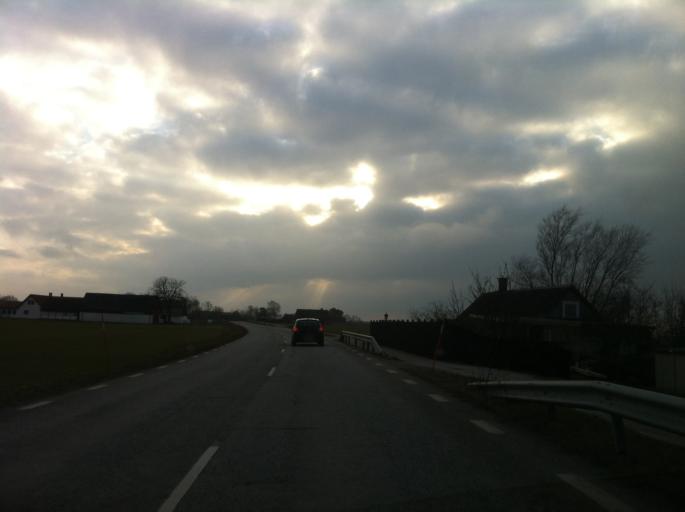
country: SE
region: Skane
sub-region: Kavlinge Kommun
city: Kaevlinge
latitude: 55.7854
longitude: 13.0784
